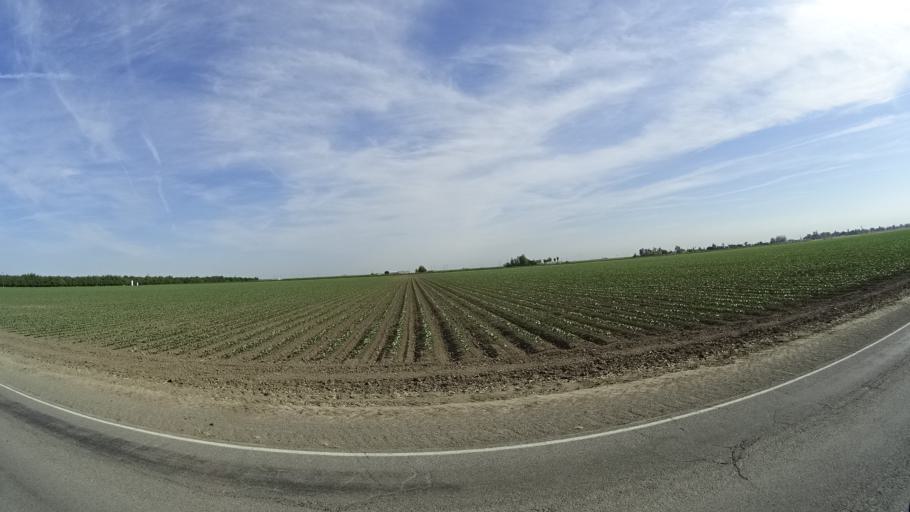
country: US
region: California
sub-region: Tulare County
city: Goshen
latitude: 36.3420
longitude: -119.4810
